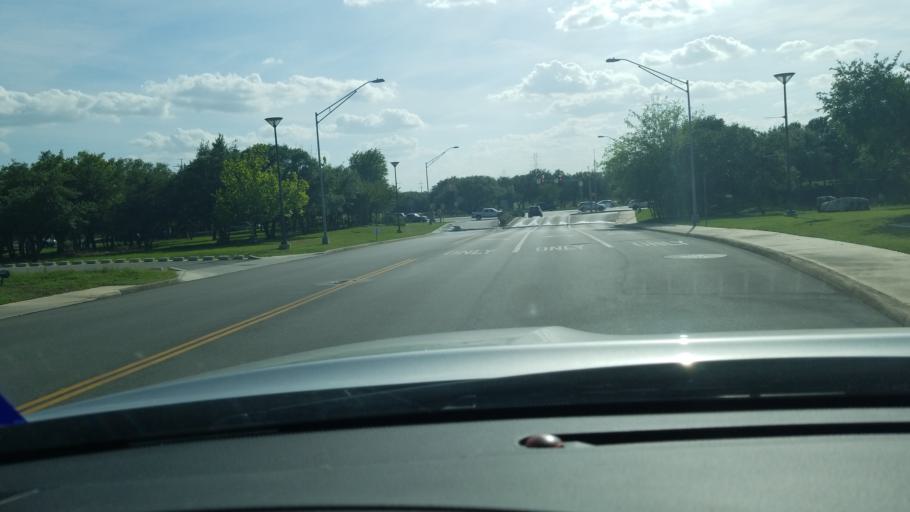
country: US
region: Texas
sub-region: Bexar County
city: Hollywood Park
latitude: 29.6211
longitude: -98.4930
